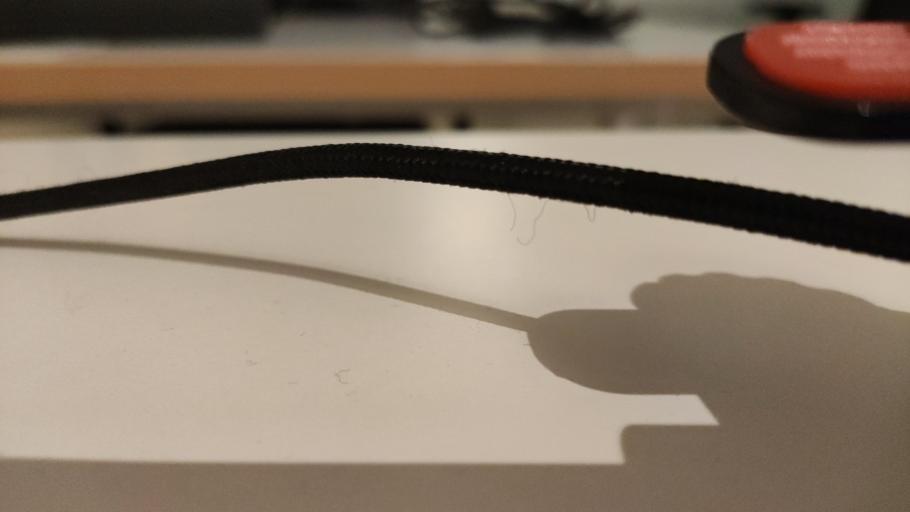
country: RU
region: Moskovskaya
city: Kurovskoye
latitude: 55.5424
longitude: 38.8731
